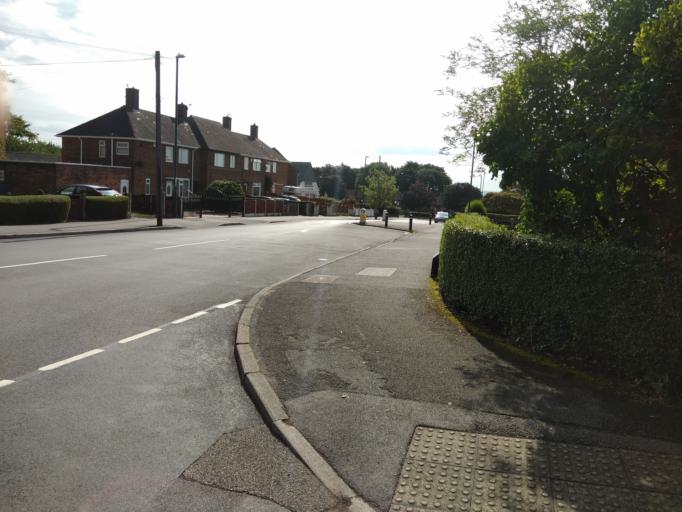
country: GB
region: England
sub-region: Nottinghamshire
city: Kimberley
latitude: 52.9742
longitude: -1.2282
